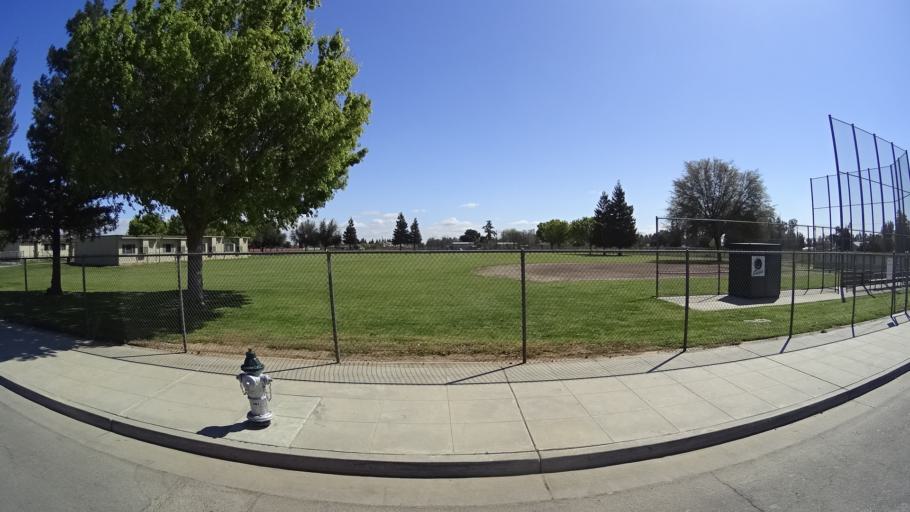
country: US
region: California
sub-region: Fresno County
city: West Park
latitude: 36.7876
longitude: -119.8759
